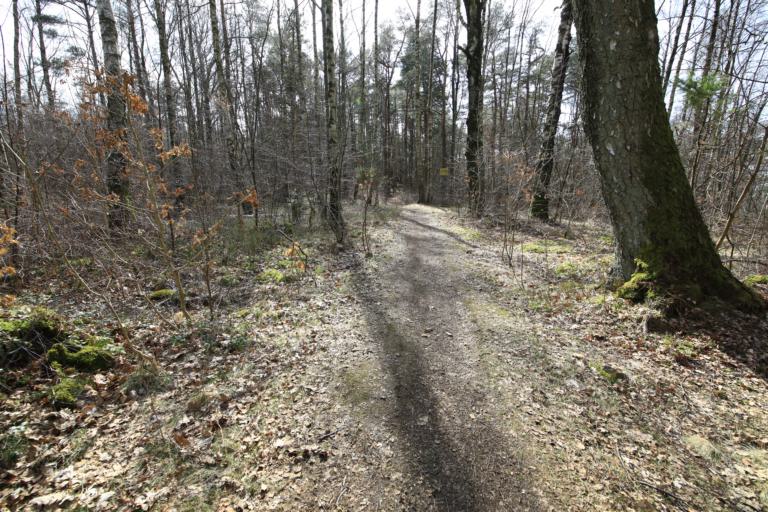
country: SE
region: Halland
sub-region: Varbergs Kommun
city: Varberg
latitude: 57.1482
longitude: 12.2867
